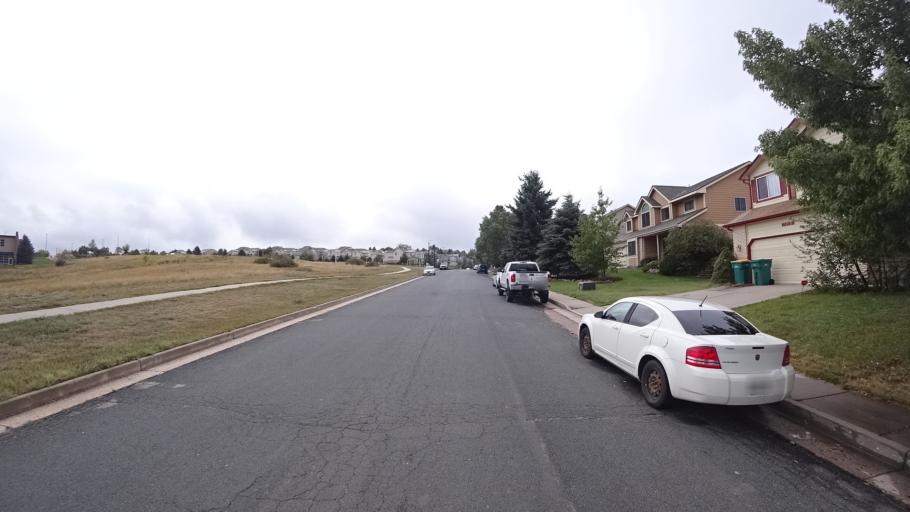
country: US
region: Colorado
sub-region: El Paso County
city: Cimarron Hills
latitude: 38.9271
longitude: -104.7571
